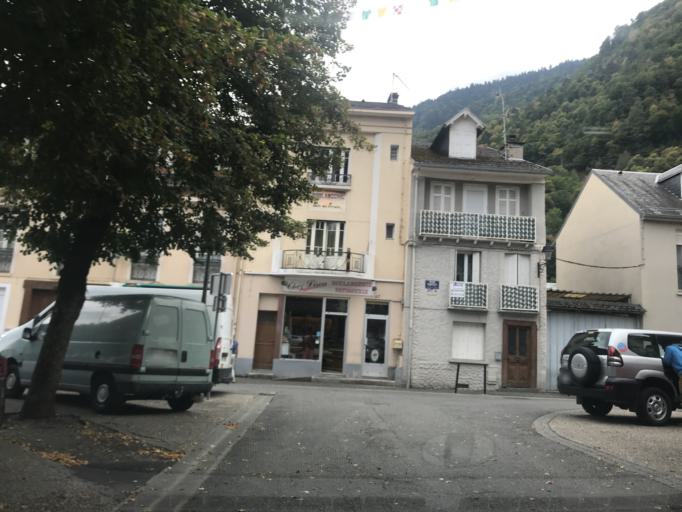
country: FR
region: Midi-Pyrenees
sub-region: Departement de la Haute-Garonne
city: Bagneres-de-Luchon
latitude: 42.7911
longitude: 0.5890
